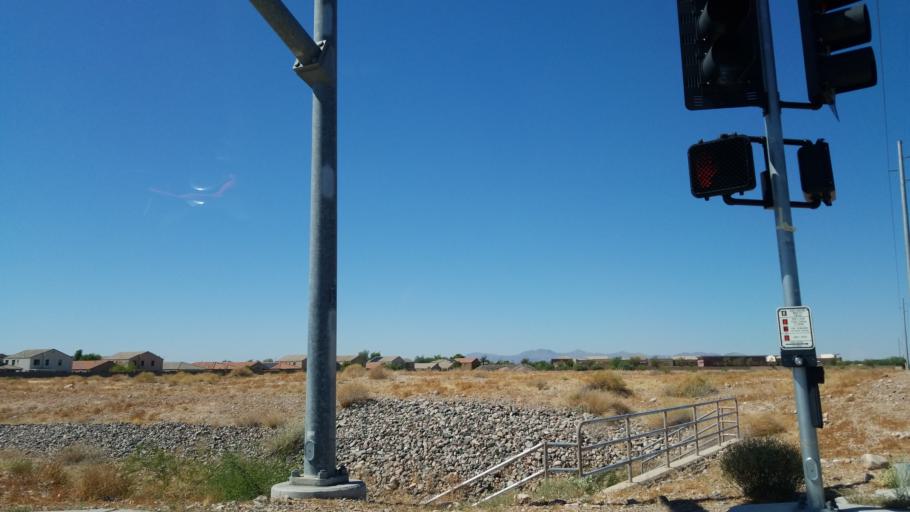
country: US
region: Arizona
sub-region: Maricopa County
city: Sun City West
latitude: 33.6816
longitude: -112.2704
